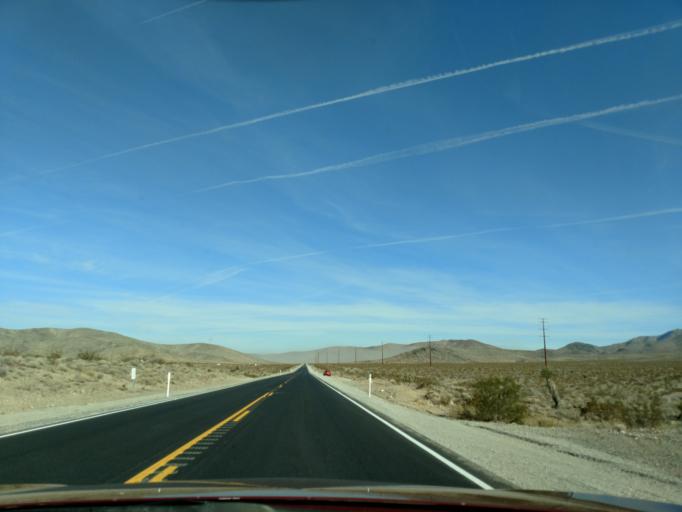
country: US
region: Nevada
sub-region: Nye County
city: Pahrump
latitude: 36.4132
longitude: -116.0692
